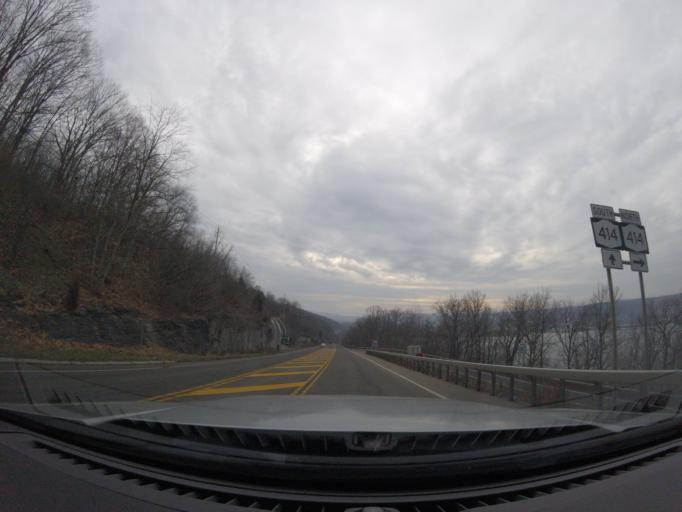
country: US
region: New York
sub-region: Schuyler County
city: Watkins Glen
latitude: 42.3958
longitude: -76.8573
